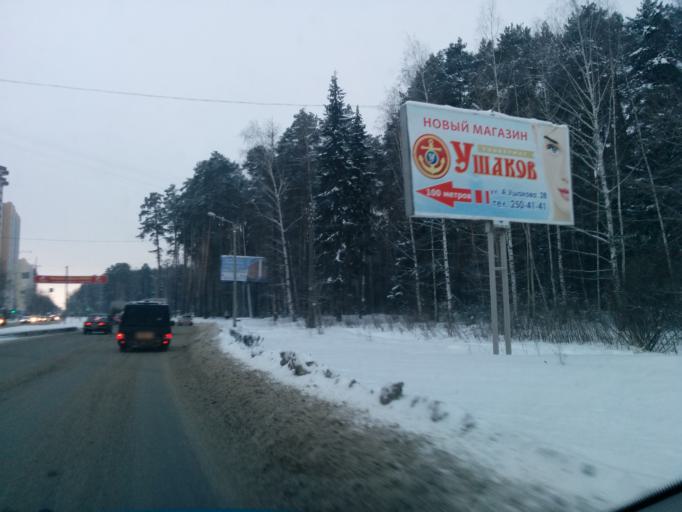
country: RU
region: Perm
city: Kondratovo
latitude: 58.0360
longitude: 56.0220
